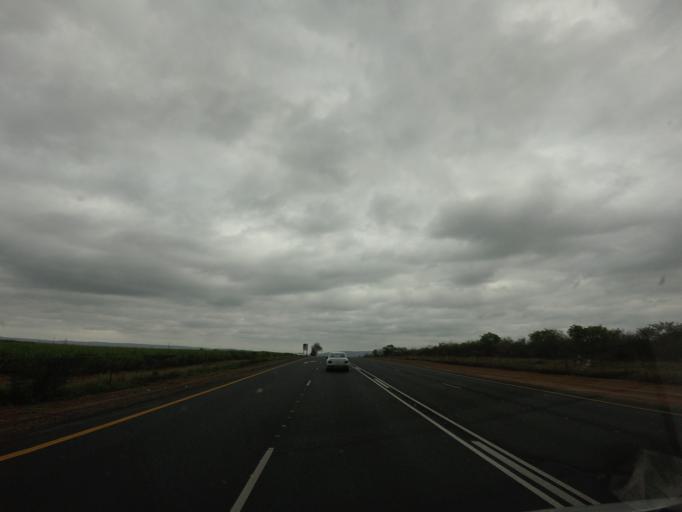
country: ZA
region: Mpumalanga
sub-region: Ehlanzeni District
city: Komatipoort
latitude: -25.4388
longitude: 31.8621
